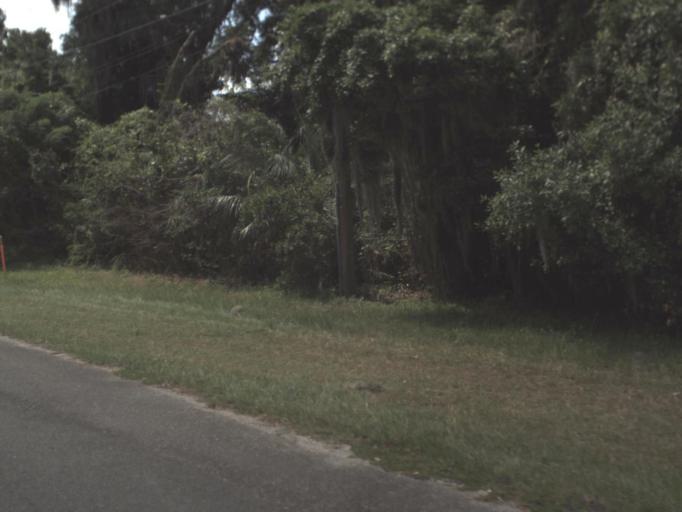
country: US
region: Florida
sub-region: Clay County
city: Green Cove Springs
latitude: 29.9924
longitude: -81.5859
